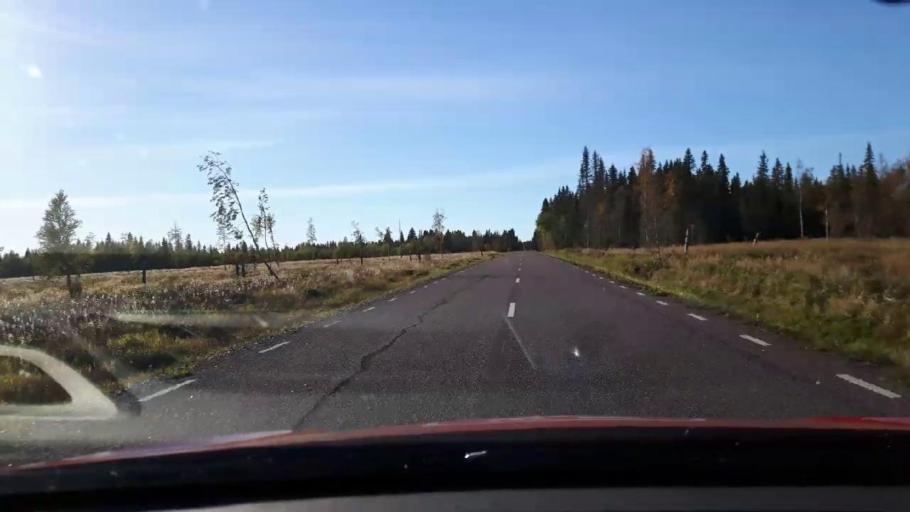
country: SE
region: Jaemtland
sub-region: Stroemsunds Kommun
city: Stroemsund
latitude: 63.8630
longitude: 15.1605
